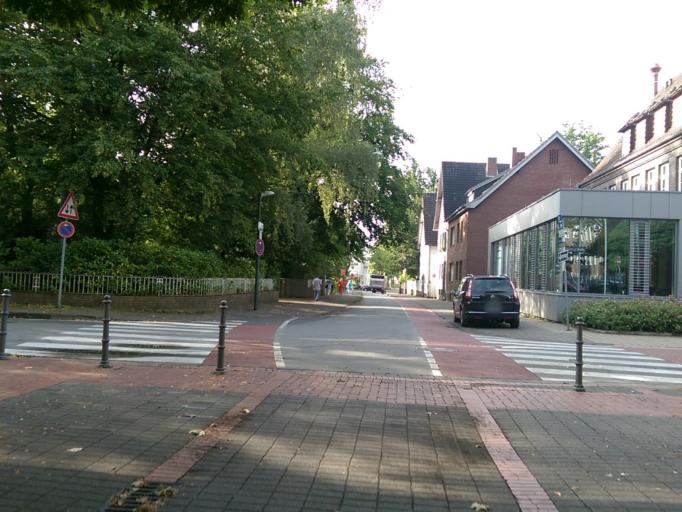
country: DE
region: North Rhine-Westphalia
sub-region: Regierungsbezirk Detmold
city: Guetersloh
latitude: 51.9055
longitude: 8.3739
